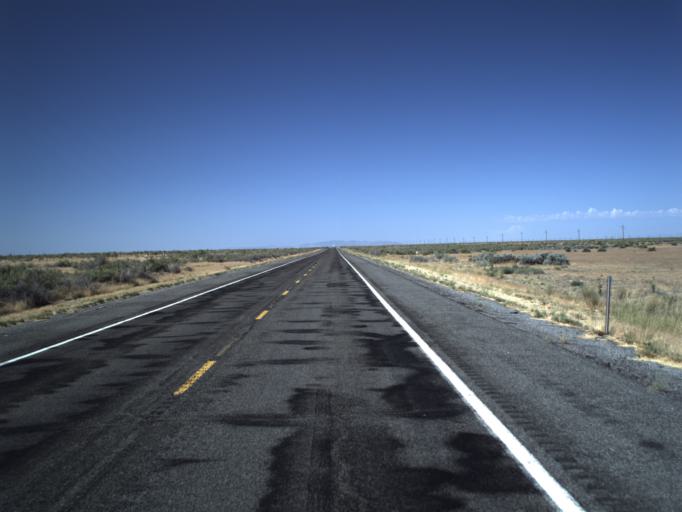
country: US
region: Utah
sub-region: Millard County
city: Delta
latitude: 39.4519
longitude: -112.4438
